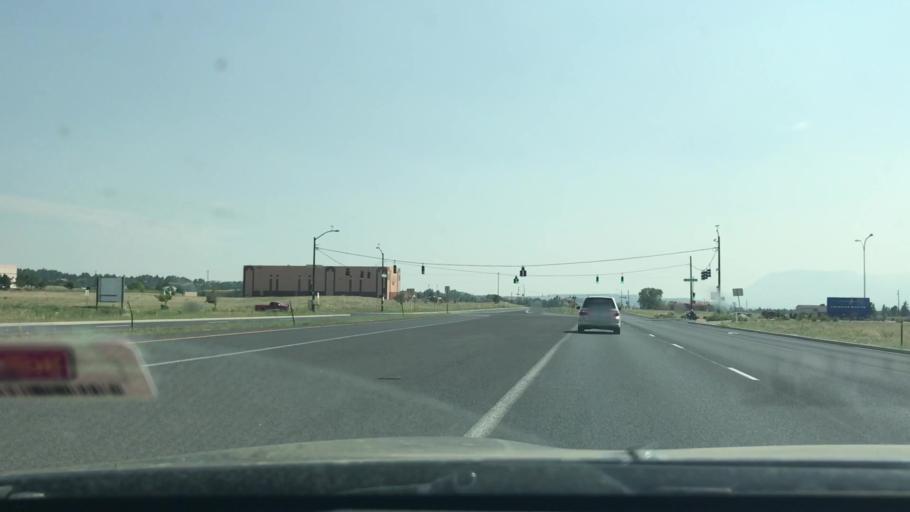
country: US
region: Colorado
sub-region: El Paso County
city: Gleneagle
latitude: 38.9841
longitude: -104.7975
